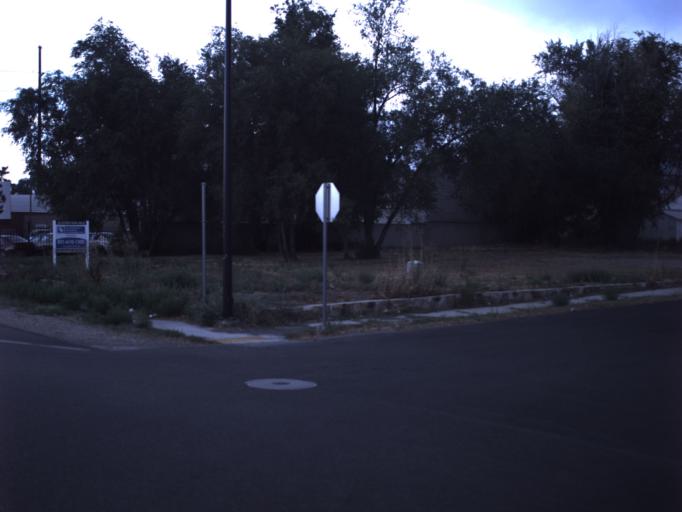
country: US
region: Utah
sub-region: Salt Lake County
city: Sandy City
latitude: 40.5909
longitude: -111.8908
